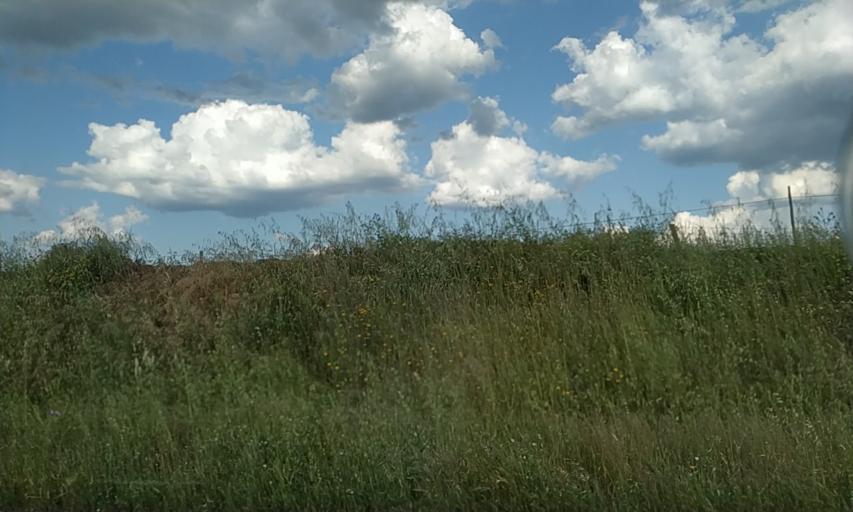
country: PT
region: Portalegre
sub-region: Portalegre
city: Portalegre
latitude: 39.2464
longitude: -7.4495
